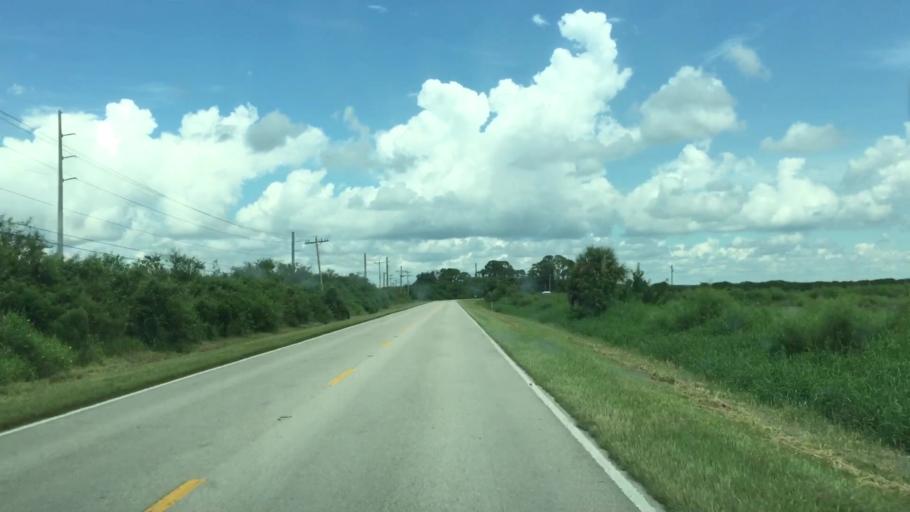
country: US
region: Florida
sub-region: Collier County
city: Immokalee
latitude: 26.3654
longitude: -81.4167
